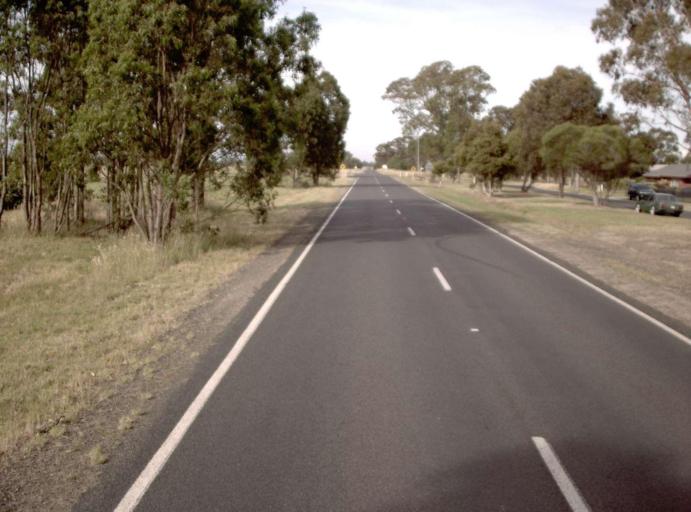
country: AU
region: Victoria
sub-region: Latrobe
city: Traralgon
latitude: -38.1206
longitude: 146.5739
